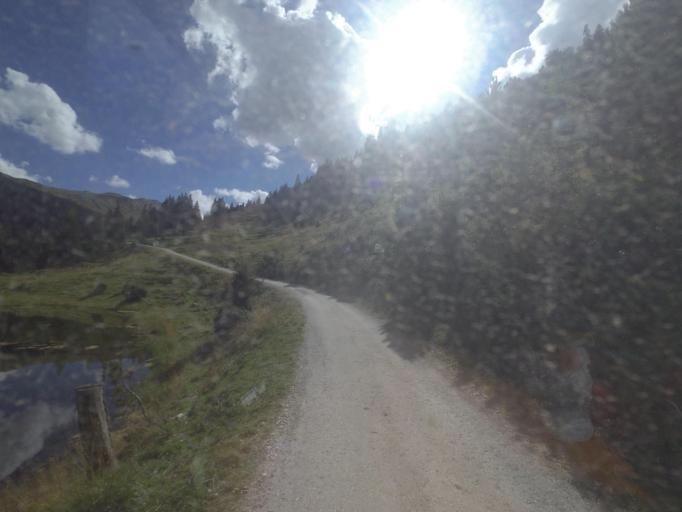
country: AT
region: Salzburg
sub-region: Politischer Bezirk Sankt Johann im Pongau
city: Kleinarl
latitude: 47.1792
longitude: 13.3541
